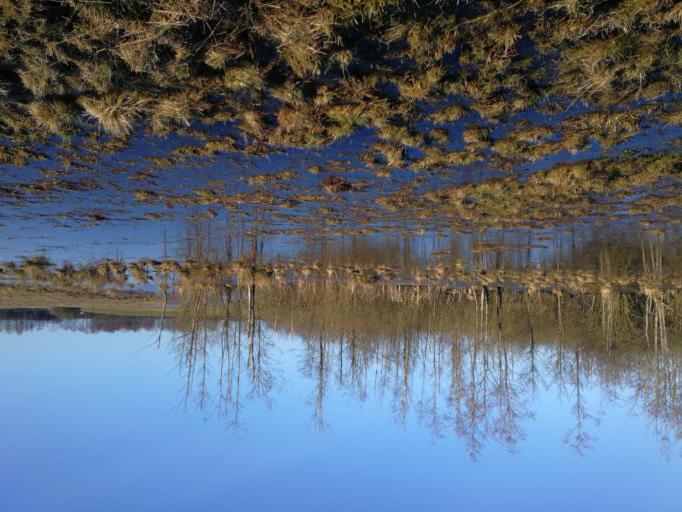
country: PL
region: Warmian-Masurian Voivodeship
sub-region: Powiat dzialdowski
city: Rybno
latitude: 53.4122
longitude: 19.9097
